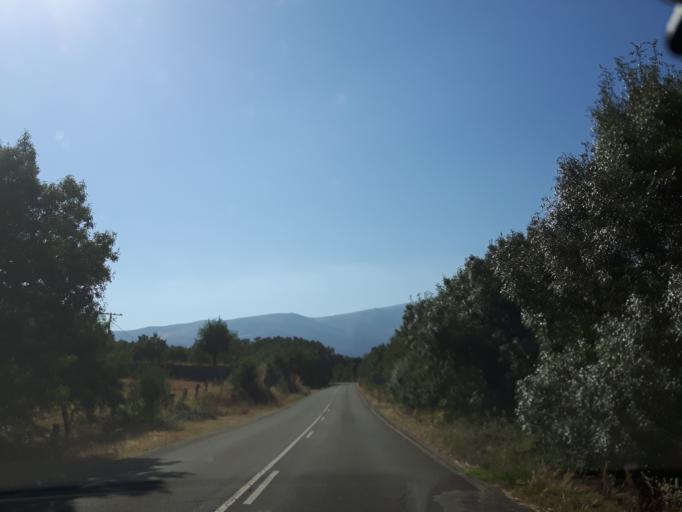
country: ES
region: Castille and Leon
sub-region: Provincia de Salamanca
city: Navalmoral de Bejar
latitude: 40.4065
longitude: -5.7996
